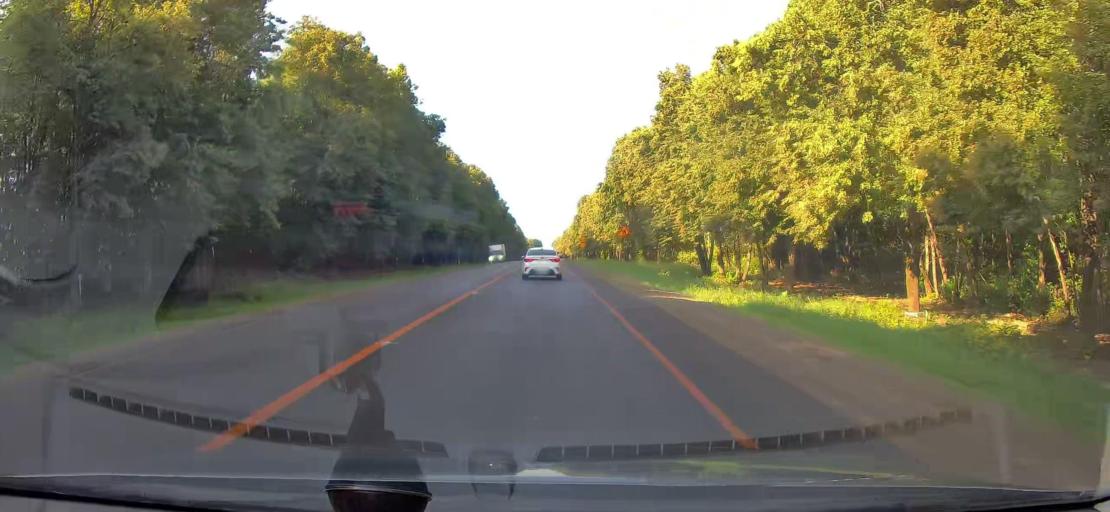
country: RU
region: Orjol
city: Spasskoye-Lutovinovo
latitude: 53.3706
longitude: 36.7324
